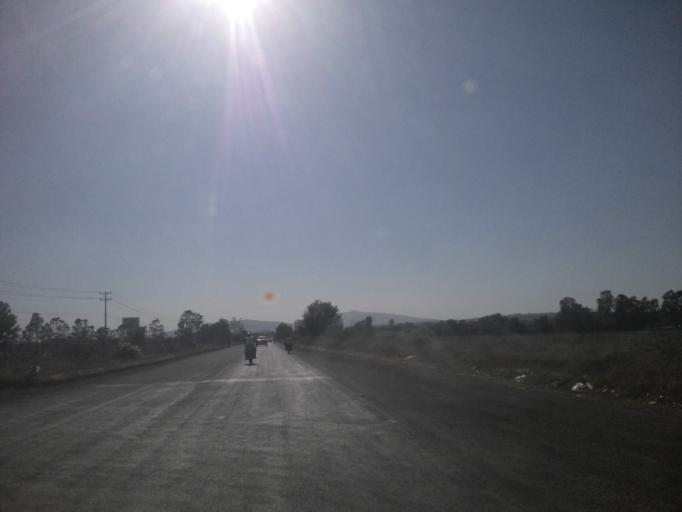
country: MX
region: Jalisco
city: Arandas
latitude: 20.7099
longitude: -102.3996
